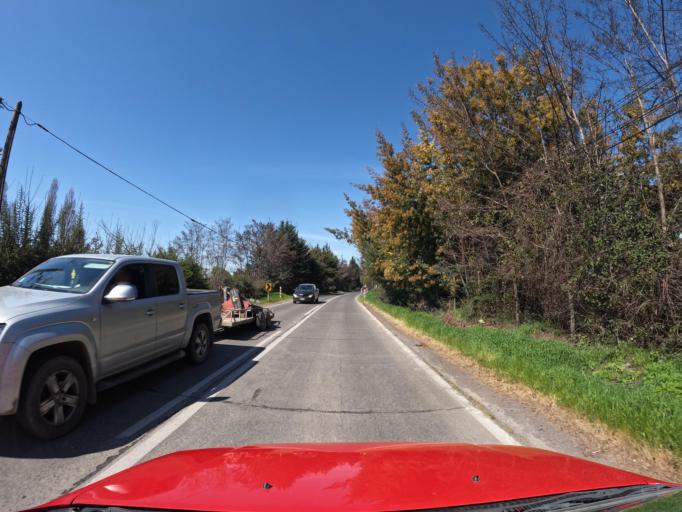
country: CL
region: Maule
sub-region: Provincia de Curico
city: Curico
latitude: -35.0086
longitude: -71.3167
